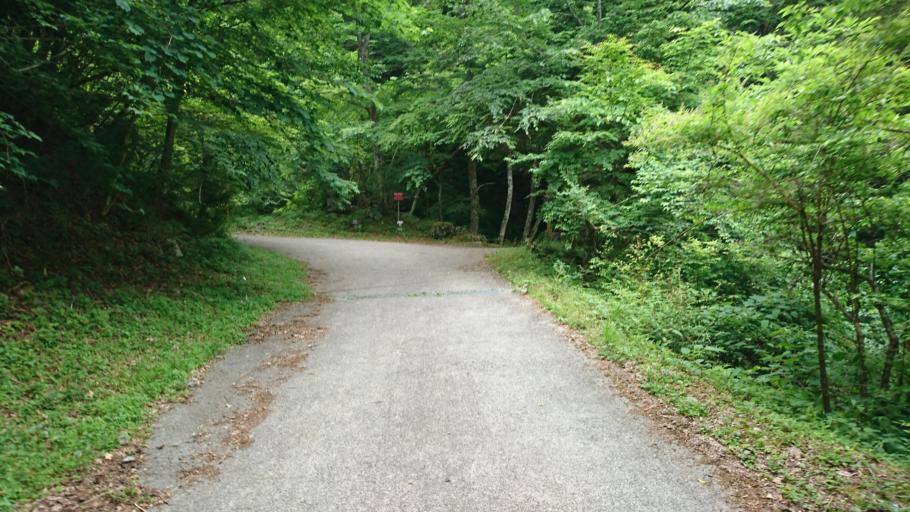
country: JP
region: Shizuoka
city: Fujinomiya
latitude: 35.3084
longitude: 138.3383
